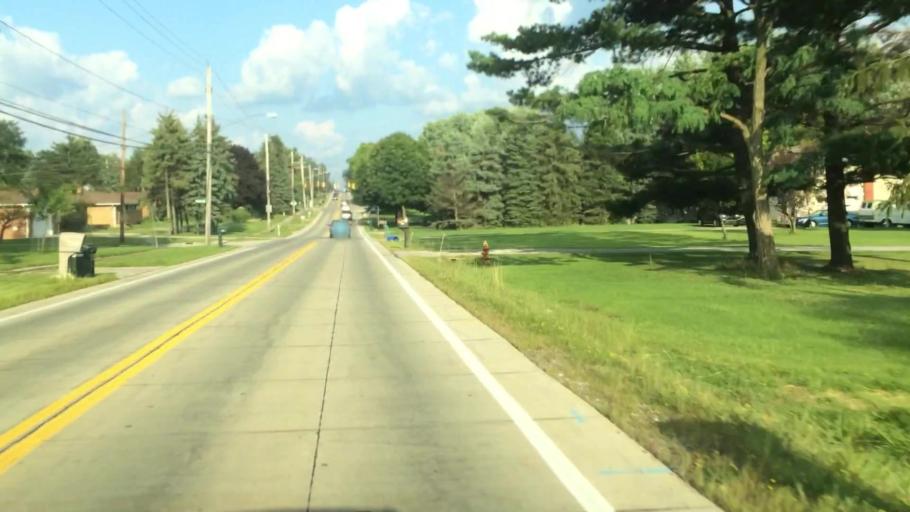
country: US
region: Ohio
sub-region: Cuyahoga County
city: North Royalton
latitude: 41.3510
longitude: -81.7066
